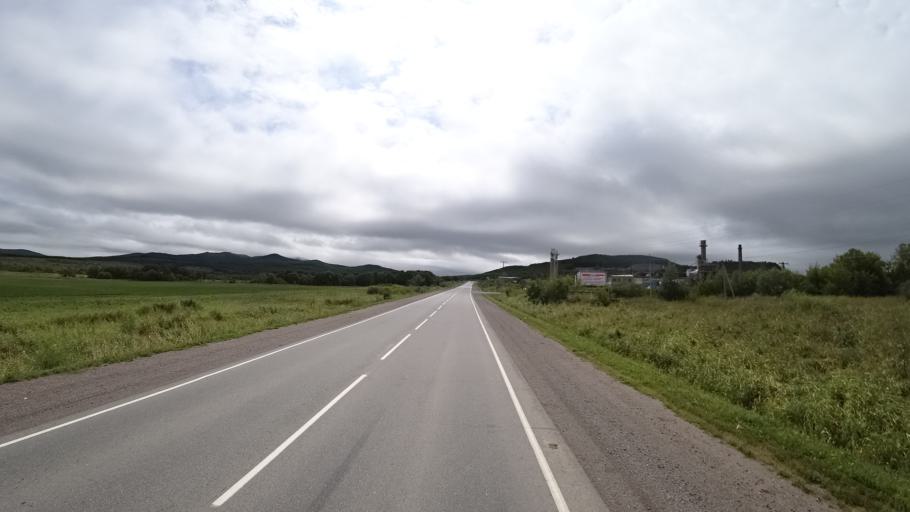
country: RU
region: Primorskiy
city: Monastyrishche
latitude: 44.1706
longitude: 132.4411
